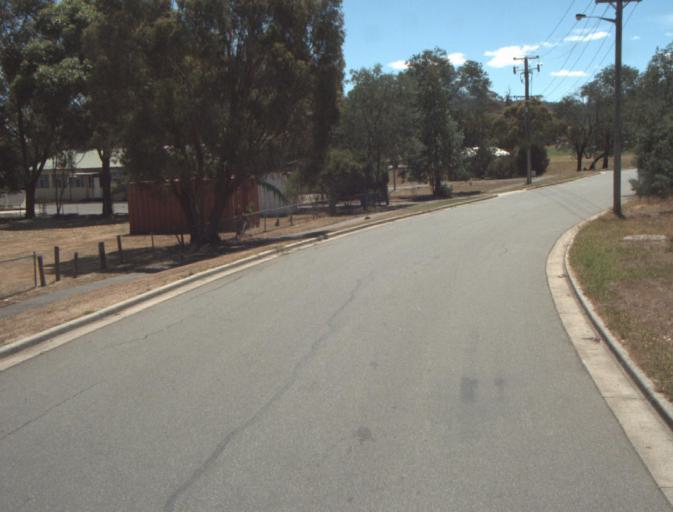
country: AU
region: Tasmania
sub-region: Launceston
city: Mayfield
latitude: -41.3763
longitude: 147.1301
